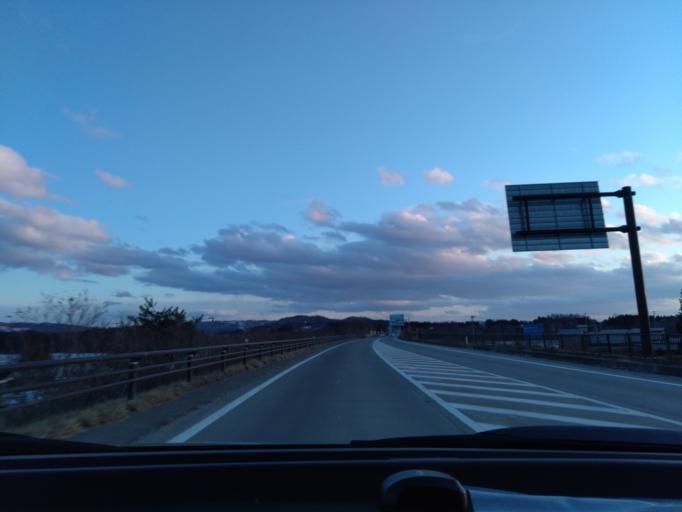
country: JP
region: Iwate
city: Hanamaki
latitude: 39.4055
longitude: 141.1386
